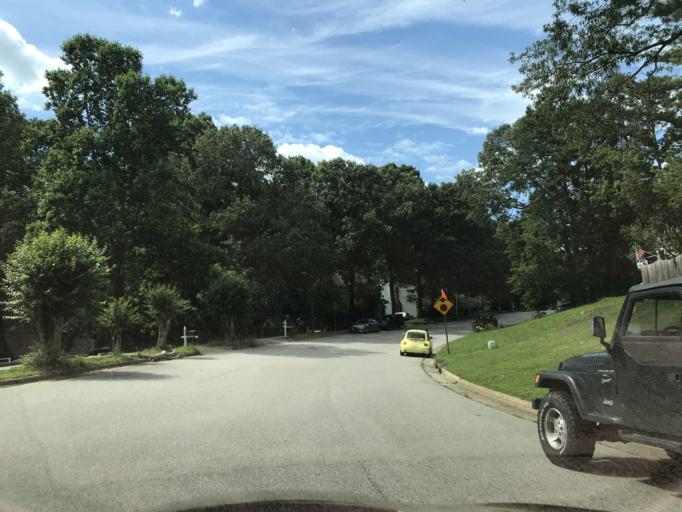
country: US
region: North Carolina
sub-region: Wake County
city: West Raleigh
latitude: 35.8812
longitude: -78.6839
